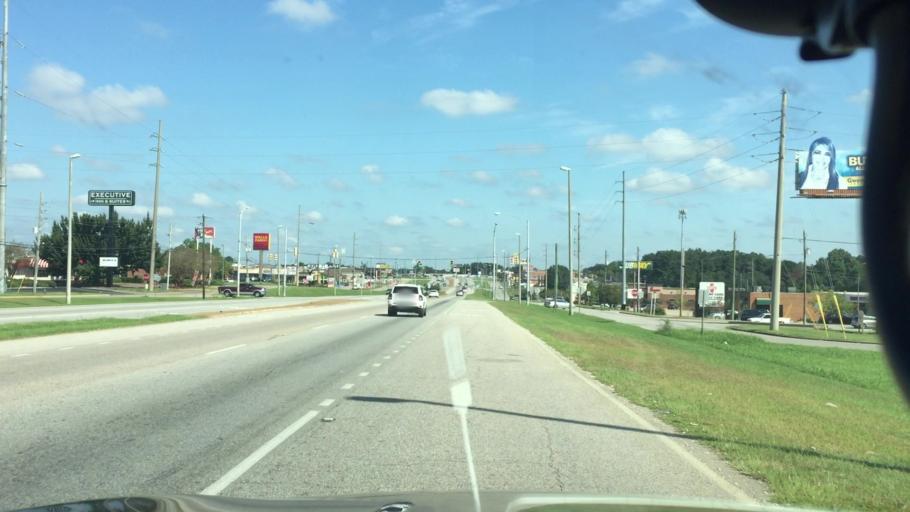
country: US
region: Alabama
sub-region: Coffee County
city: Enterprise
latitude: 31.3162
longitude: -85.8301
